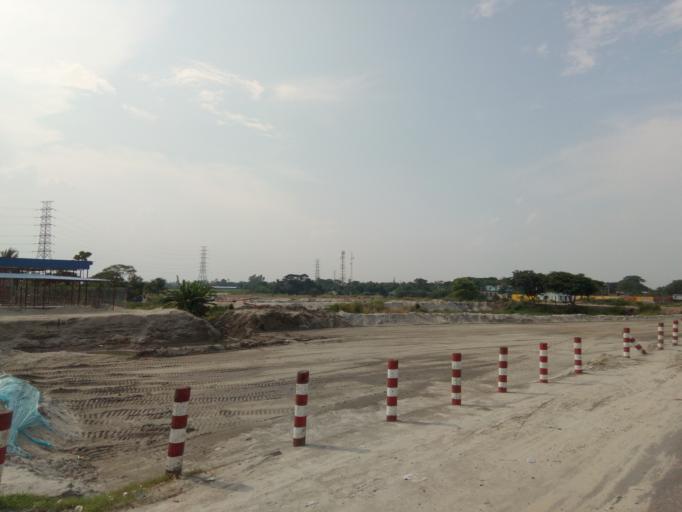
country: BD
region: Dhaka
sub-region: Dhaka
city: Dhaka
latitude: 23.6496
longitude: 90.3502
